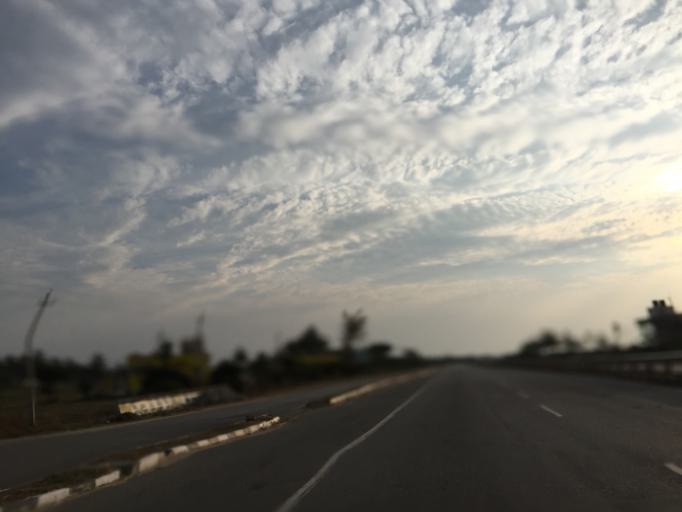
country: IN
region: Karnataka
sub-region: Kolar
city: Kolar
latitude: 13.1210
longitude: 78.1491
